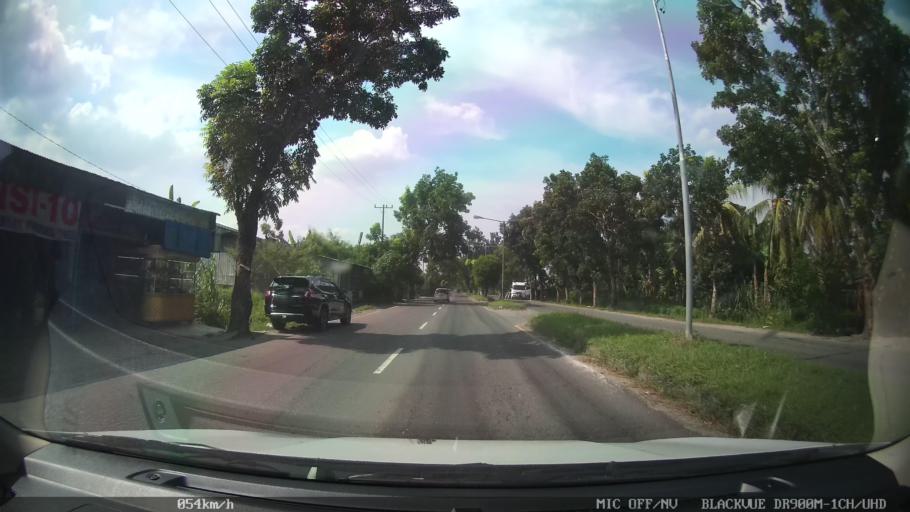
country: ID
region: North Sumatra
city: Binjai
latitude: 3.6143
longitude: 98.5342
